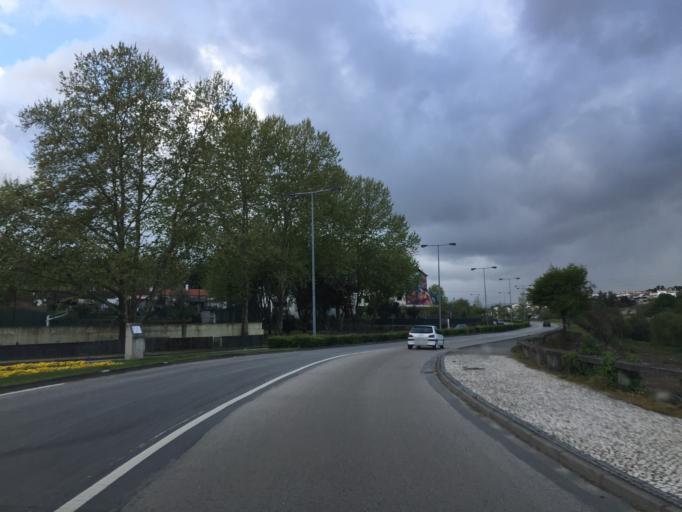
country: PT
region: Viseu
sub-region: Viseu
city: Viseu
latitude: 40.6629
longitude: -7.9204
